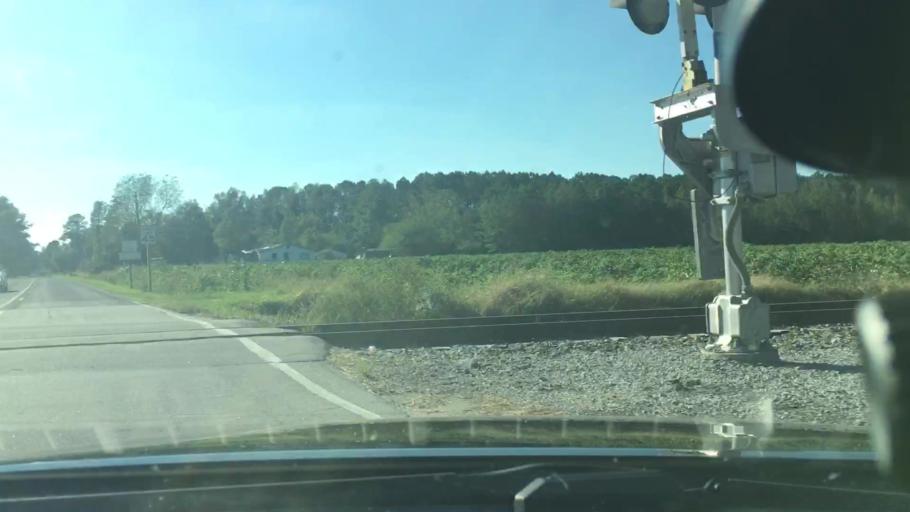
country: US
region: North Carolina
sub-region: Craven County
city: Vanceboro
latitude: 35.3388
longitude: -77.1513
